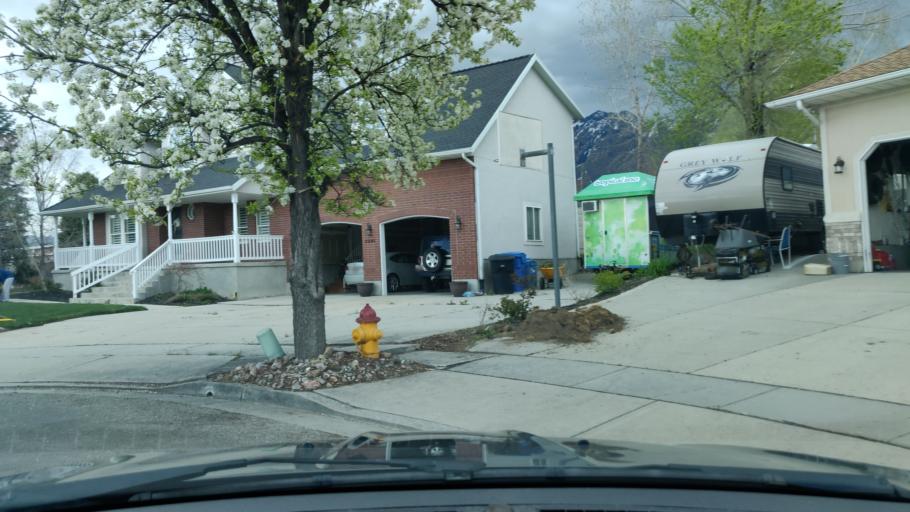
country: US
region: Utah
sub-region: Salt Lake County
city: Cottonwood Heights
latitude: 40.6275
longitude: -111.8280
